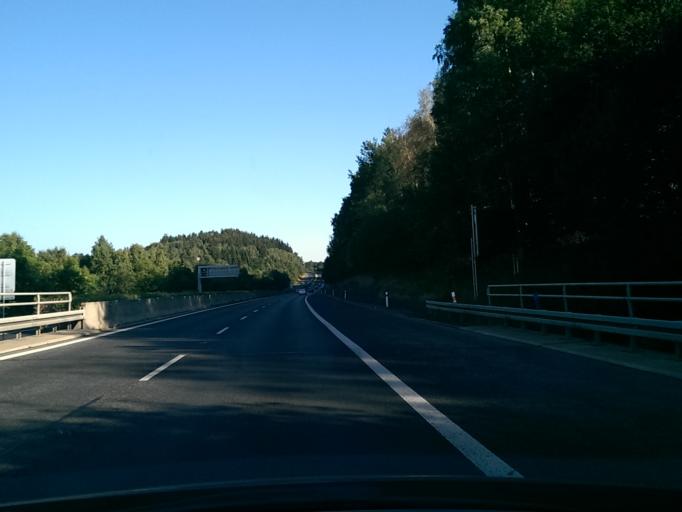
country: CZ
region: Liberecky
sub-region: Okres Liberec
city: Liberec
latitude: 50.7181
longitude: 15.0720
